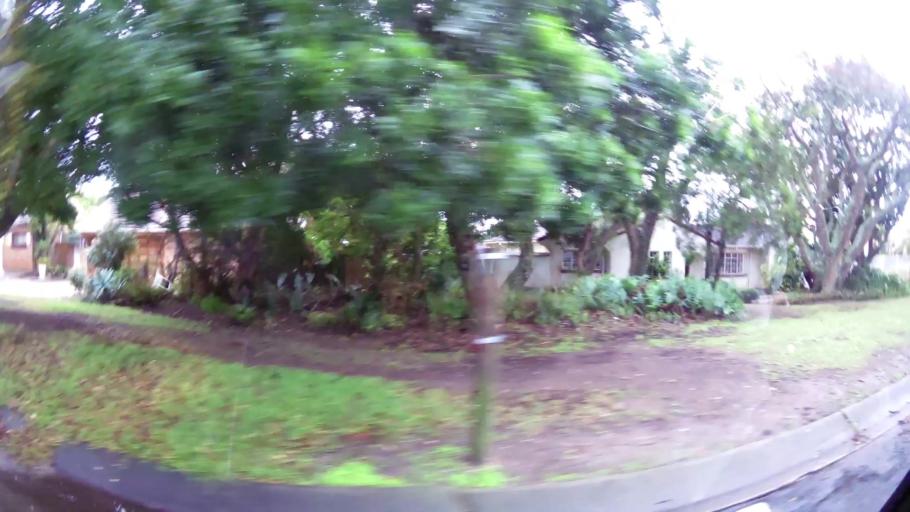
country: ZA
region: Eastern Cape
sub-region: Nelson Mandela Bay Metropolitan Municipality
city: Port Elizabeth
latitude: -33.9951
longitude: 25.5612
